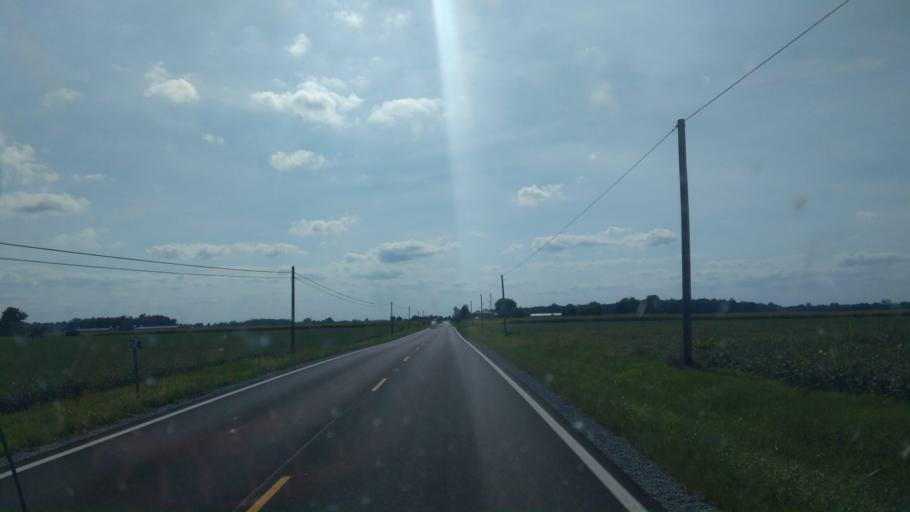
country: US
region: Ohio
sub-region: Hardin County
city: Forest
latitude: 40.6972
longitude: -83.4707
